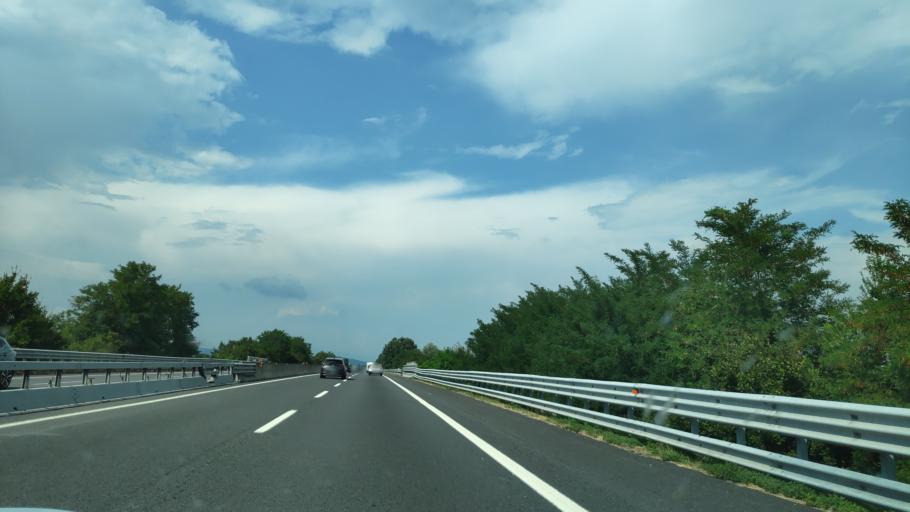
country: IT
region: Tuscany
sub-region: Province of Arezzo
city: Marciano della Chiana
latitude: 43.2937
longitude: 11.7636
